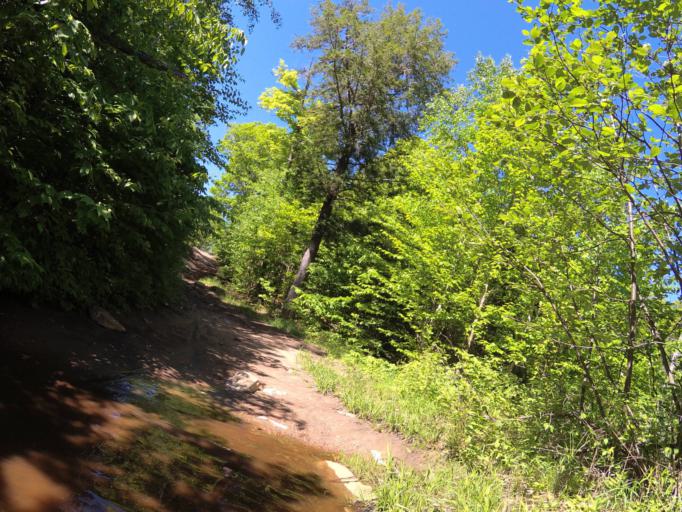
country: CA
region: Ontario
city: Renfrew
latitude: 45.0640
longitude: -77.0774
